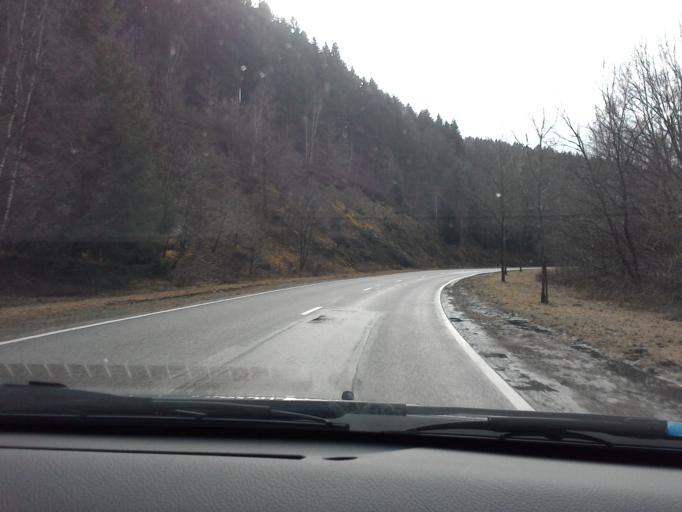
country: BE
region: Wallonia
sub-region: Province de Liege
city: Trois-Ponts
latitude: 50.3626
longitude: 5.8885
